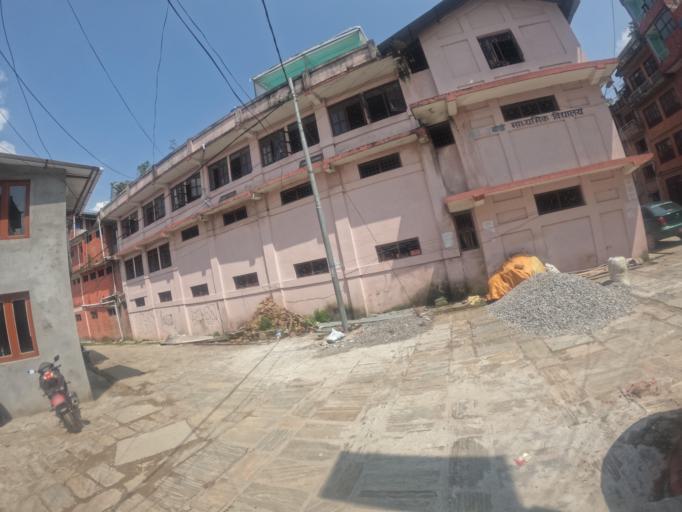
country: NP
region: Central Region
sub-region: Bagmati Zone
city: Bhaktapur
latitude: 27.6913
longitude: 85.3872
